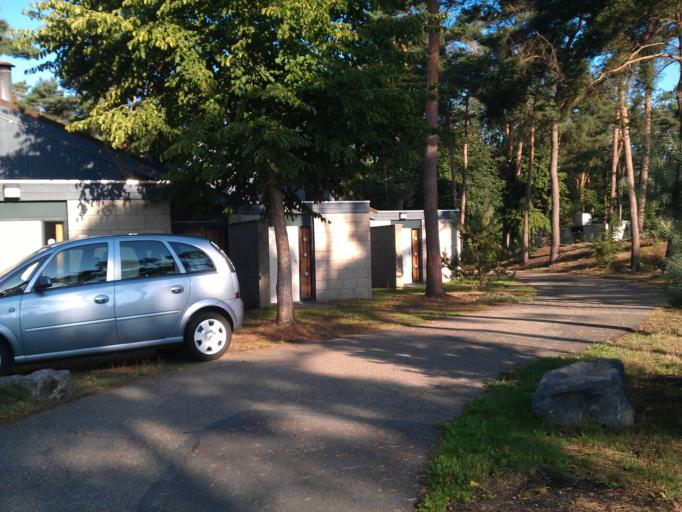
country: NL
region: North Brabant
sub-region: Gemeente Bladel en Netersel
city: Bladel
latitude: 51.3428
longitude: 5.2506
